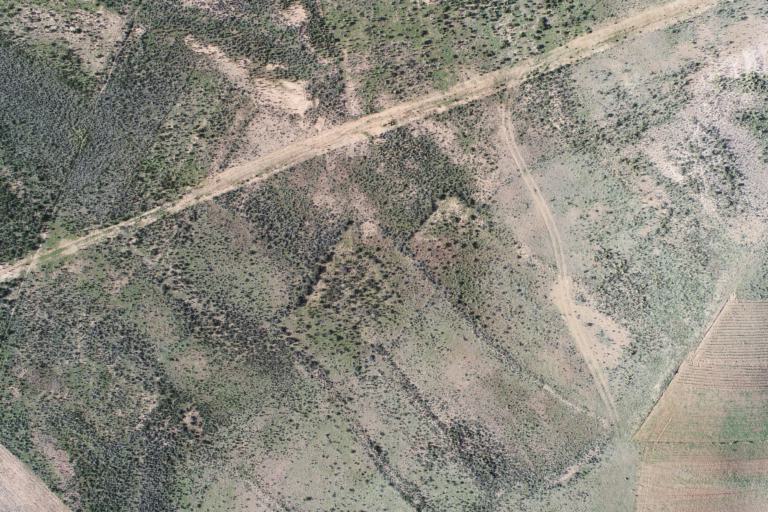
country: BO
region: La Paz
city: Curahuara de Carangas
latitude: -17.2985
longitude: -68.4950
